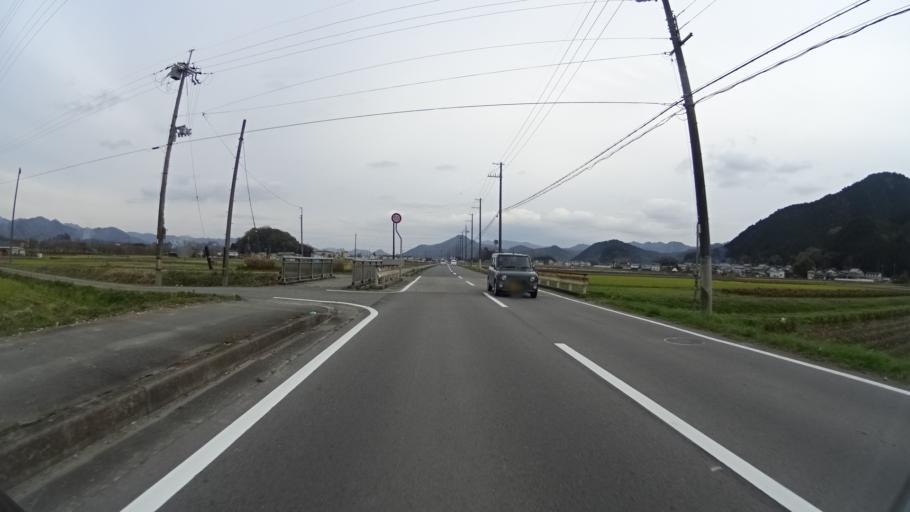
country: JP
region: Hyogo
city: Sasayama
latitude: 35.0636
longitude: 135.2091
